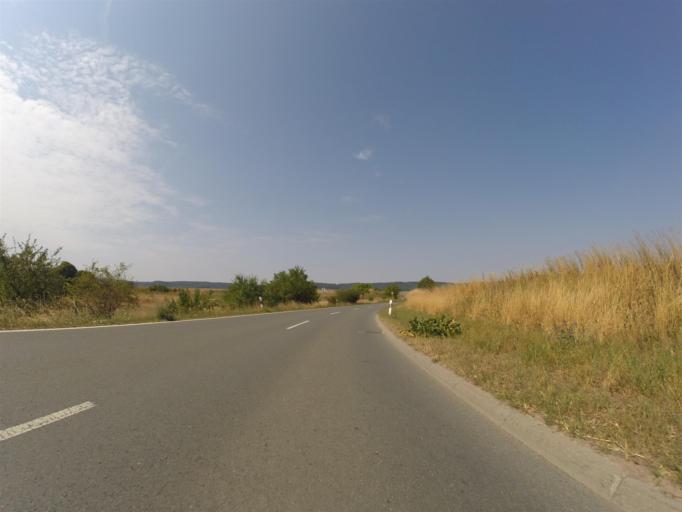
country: DE
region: Thuringia
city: Schloben
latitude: 50.8853
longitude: 11.6914
